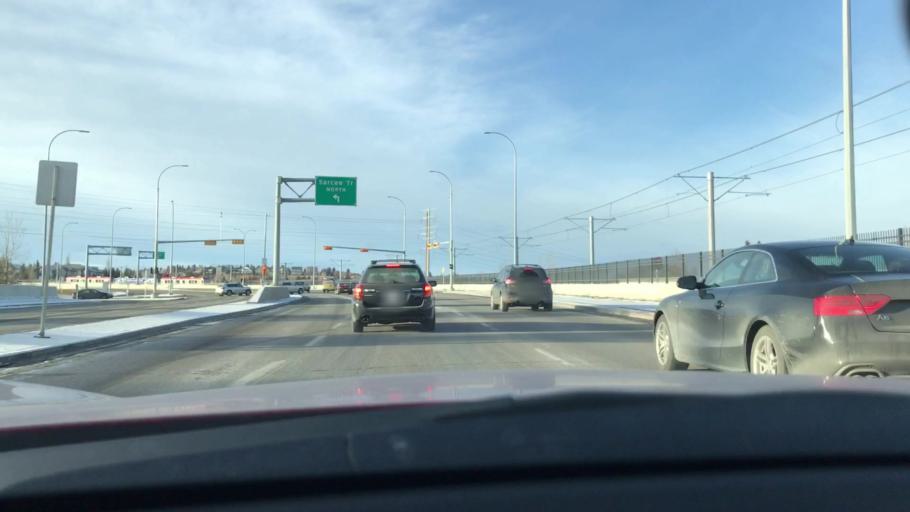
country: CA
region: Alberta
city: Calgary
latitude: 51.0390
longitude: -114.1609
